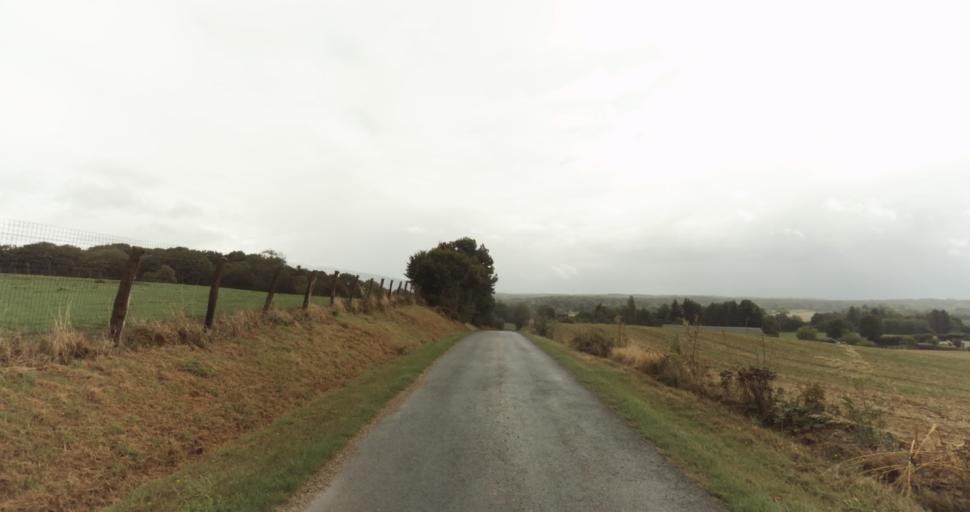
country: FR
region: Lower Normandy
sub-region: Departement de l'Orne
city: Sainte-Gauburge-Sainte-Colombe
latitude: 48.6960
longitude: 0.4084
